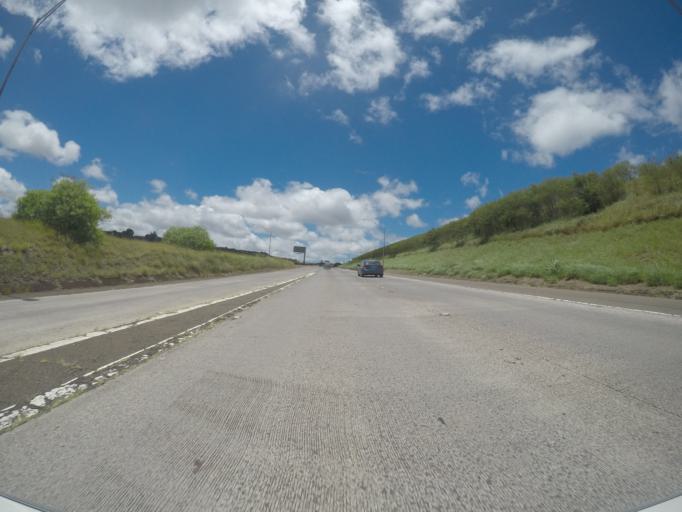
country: US
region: Hawaii
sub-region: Honolulu County
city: Pearl City, Manana
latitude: 21.4035
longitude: -157.9881
